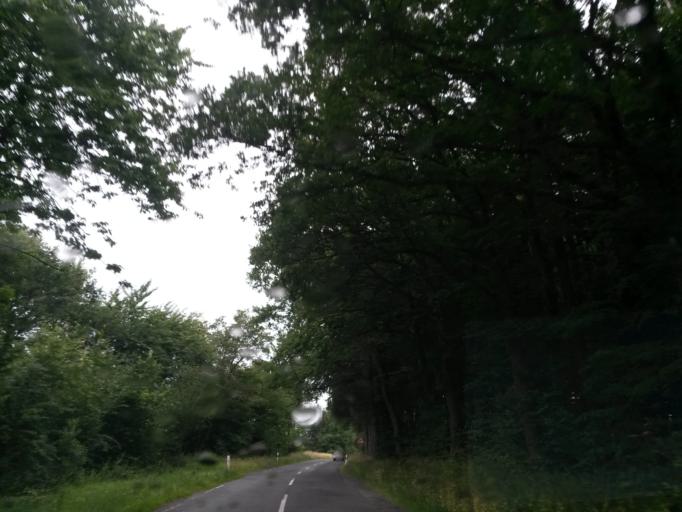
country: DE
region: North Rhine-Westphalia
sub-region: Regierungsbezirk Koln
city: Much
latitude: 50.9226
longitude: 7.3775
